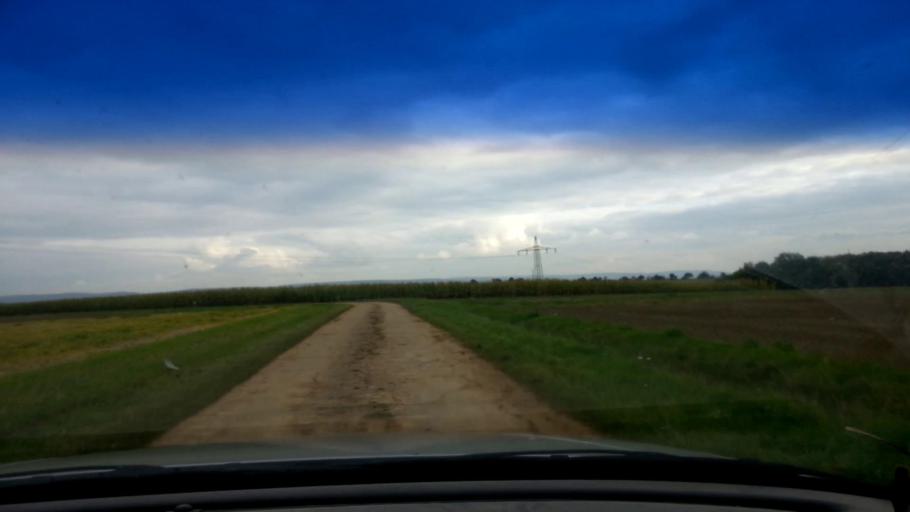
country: DE
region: Bavaria
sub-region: Upper Franconia
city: Zapfendorf
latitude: 49.9945
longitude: 10.9344
